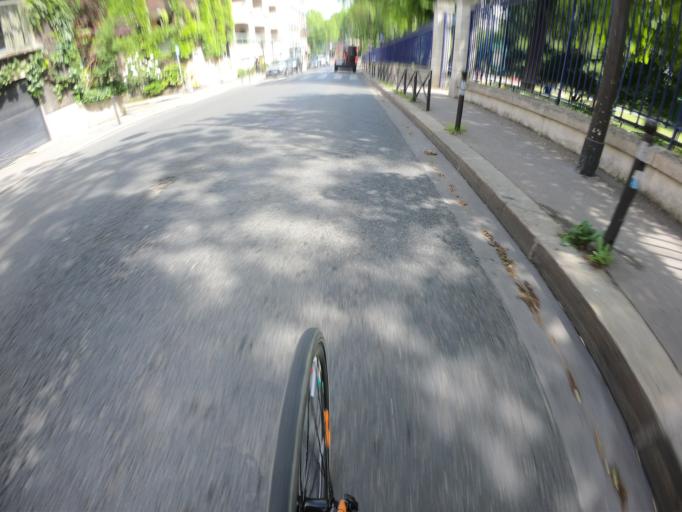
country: FR
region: Ile-de-France
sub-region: Departement du Val-de-Marne
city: Gentilly
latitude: 48.8232
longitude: 2.3357
